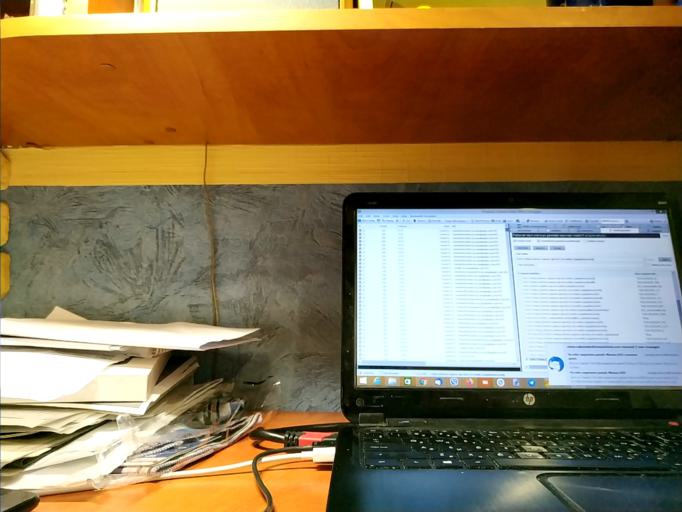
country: RU
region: Tverskaya
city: Spirovo
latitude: 57.4661
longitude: 35.0731
